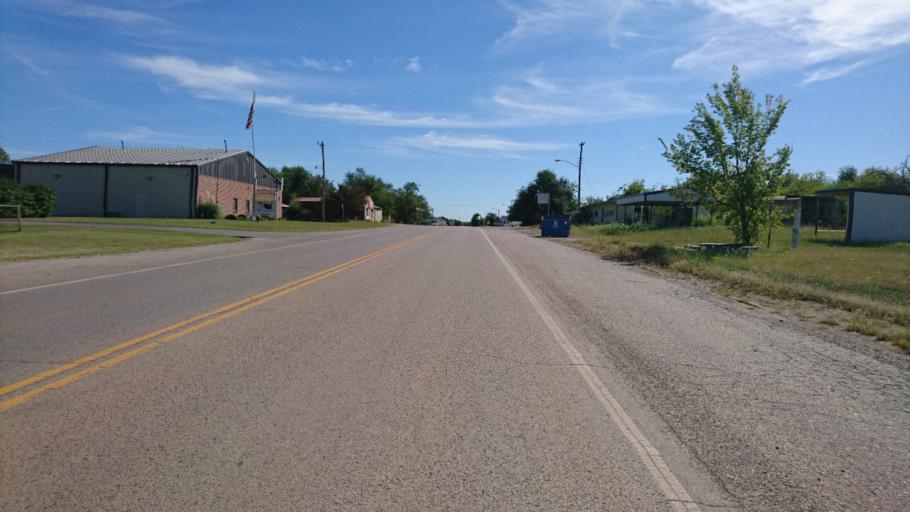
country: US
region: Oklahoma
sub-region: Lincoln County
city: Stroud
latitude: 35.7135
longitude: -96.7652
